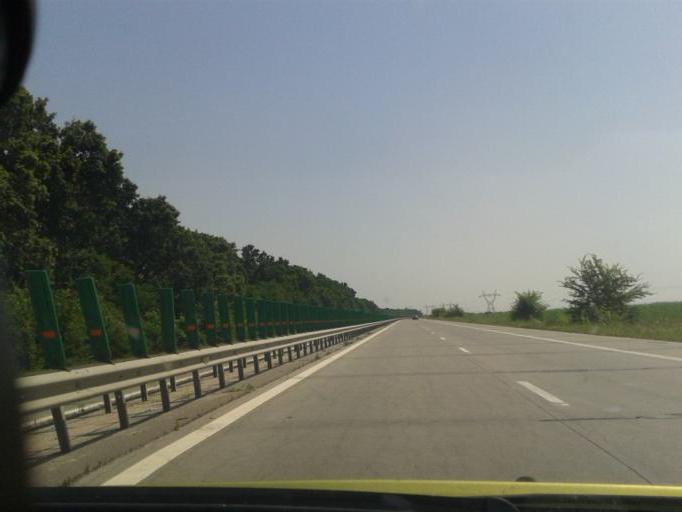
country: RO
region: Calarasi
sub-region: Comuna Belciugatele
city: Belciugatele
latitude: 44.4500
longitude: 26.4396
